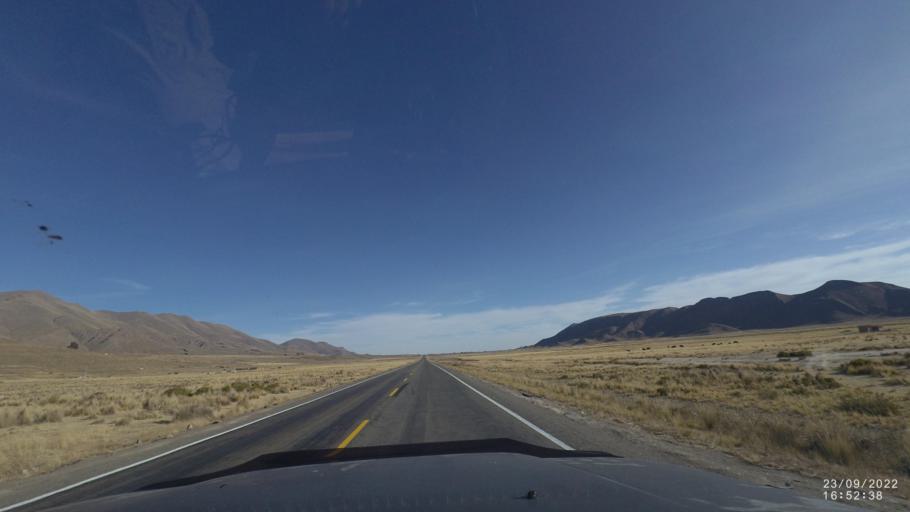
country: BO
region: Oruro
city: Poopo
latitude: -18.4344
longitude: -66.9731
